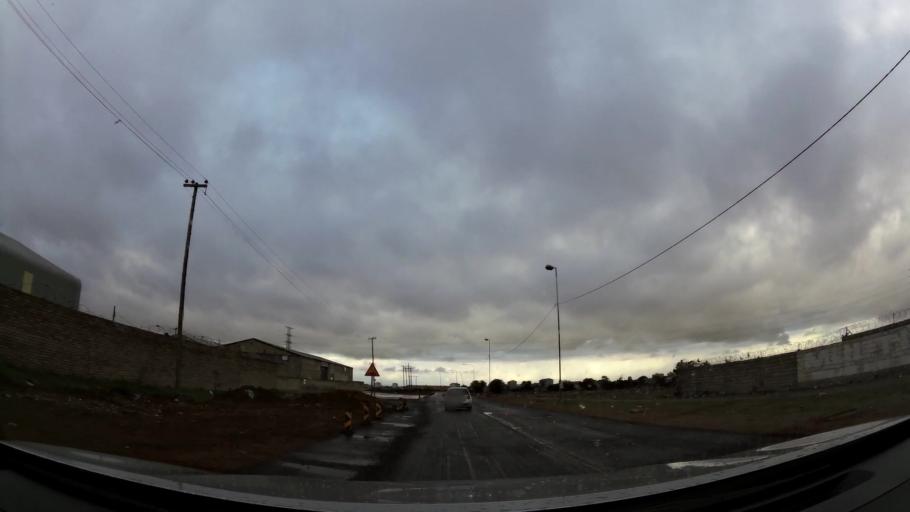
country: ZA
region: Eastern Cape
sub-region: Nelson Mandela Bay Metropolitan Municipality
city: Port Elizabeth
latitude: -33.8949
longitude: 25.5479
